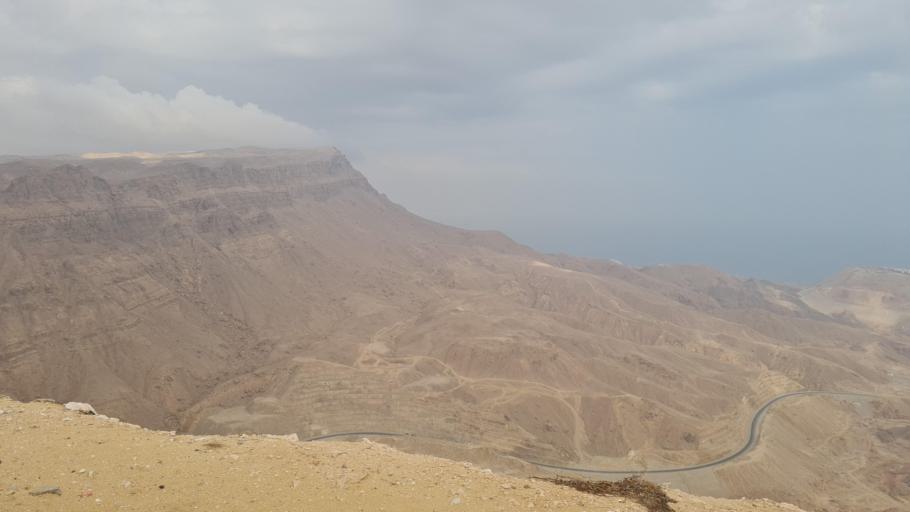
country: EG
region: As Suways
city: Ain Sukhna
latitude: 29.4471
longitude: 32.4124
